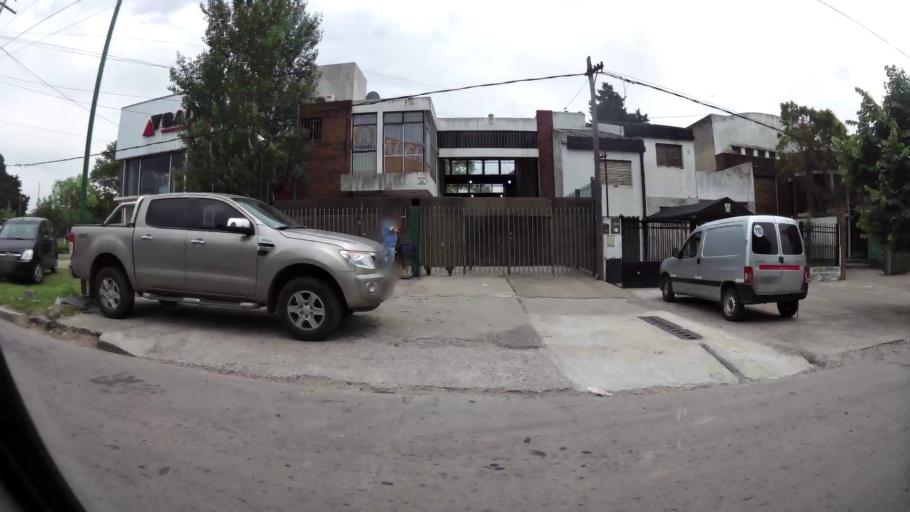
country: AR
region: Buenos Aires
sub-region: Partido de La Plata
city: La Plata
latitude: -34.8938
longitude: -57.9864
